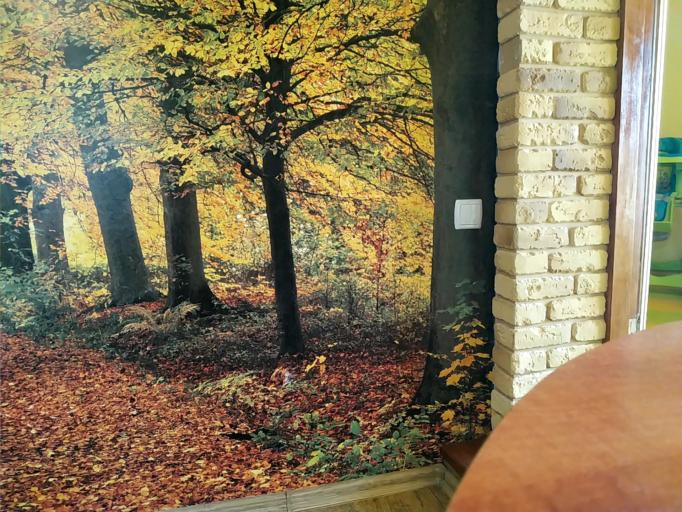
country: RU
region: Arkhangelskaya
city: Onega
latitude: 63.7535
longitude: 38.0767
